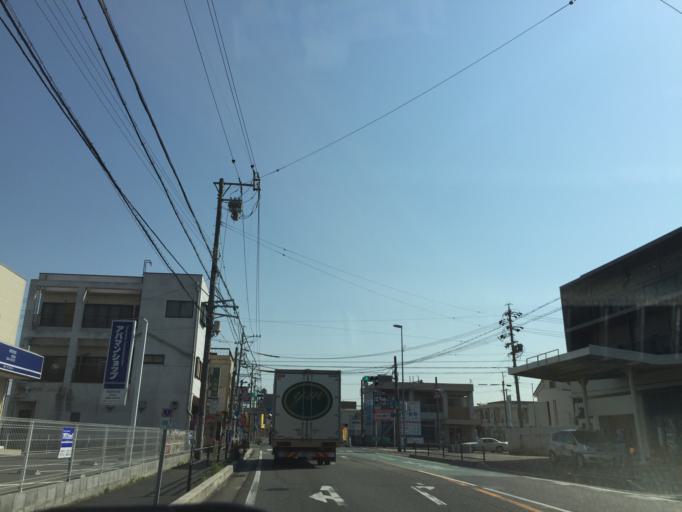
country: JP
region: Mie
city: Yokkaichi
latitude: 35.0107
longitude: 136.6577
